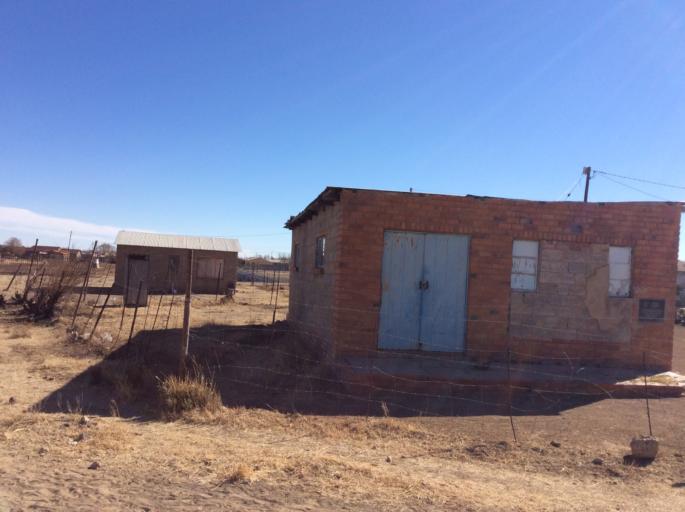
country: ZA
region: Orange Free State
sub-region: Lejweleputswa District Municipality
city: Brandfort
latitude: -28.7353
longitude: 26.1121
